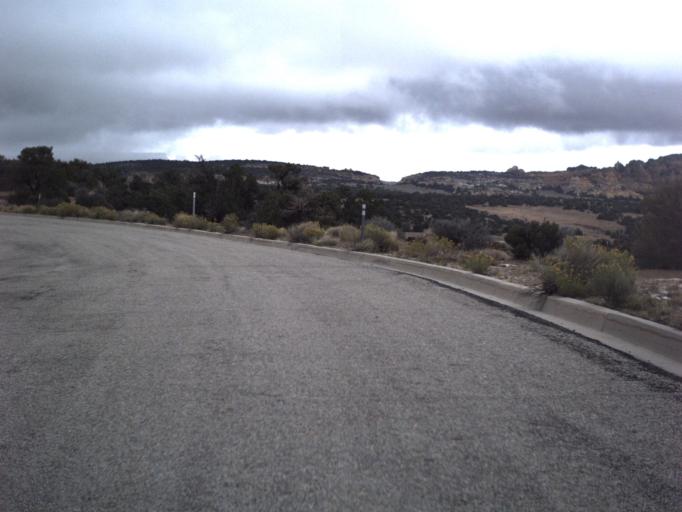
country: US
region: Utah
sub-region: Emery County
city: Ferron
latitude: 38.8609
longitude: -110.8116
